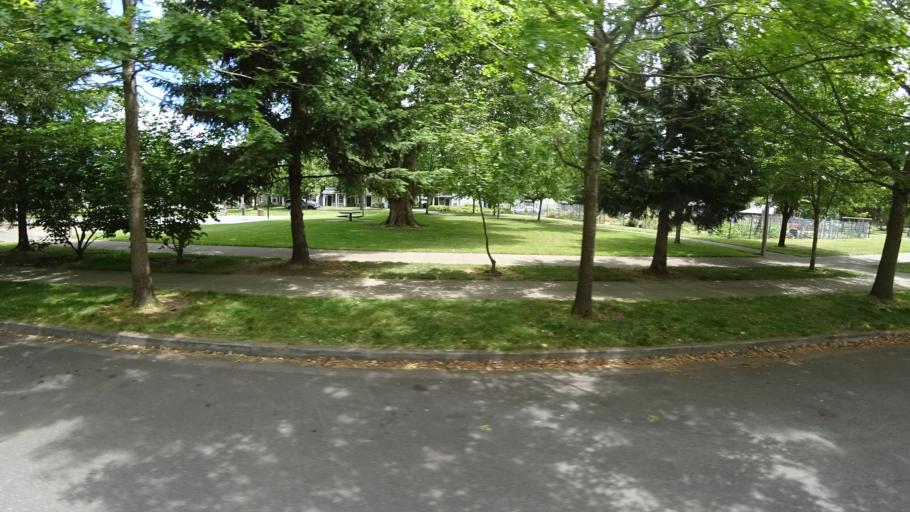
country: US
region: Washington
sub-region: Clark County
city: Vancouver
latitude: 45.5904
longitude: -122.7169
